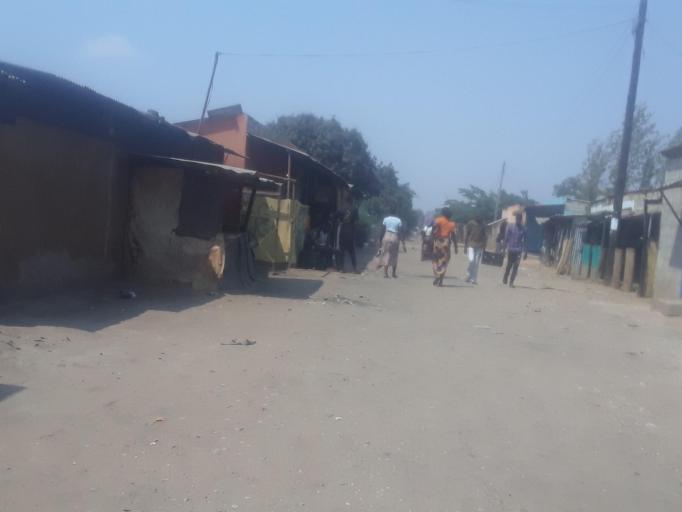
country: ZM
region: Lusaka
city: Lusaka
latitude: -15.3516
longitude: 28.2884
